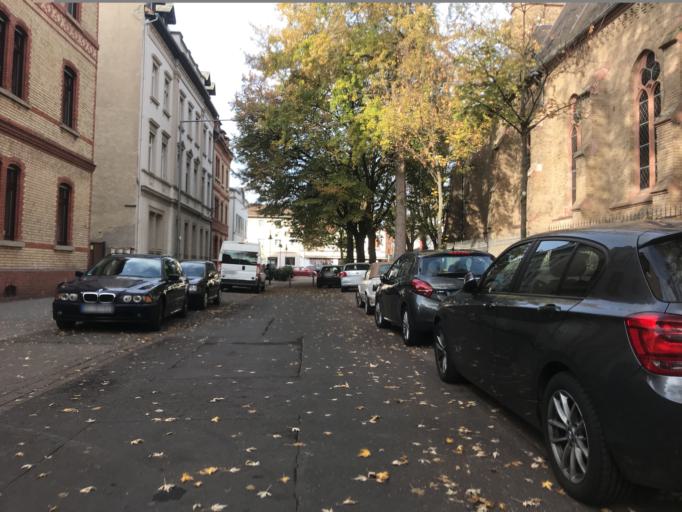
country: DE
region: Hesse
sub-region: Regierungsbezirk Darmstadt
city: Wiesbaden
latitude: 50.0393
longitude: 8.2417
